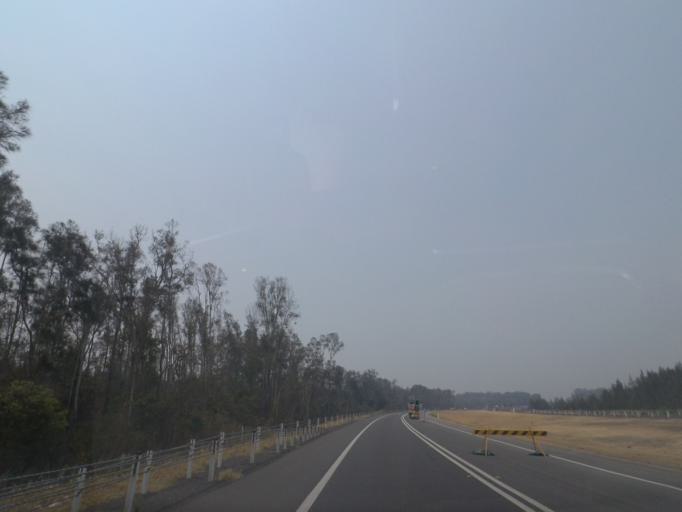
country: AU
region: New South Wales
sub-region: Ballina
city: Ballina
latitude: -28.8691
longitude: 153.4921
